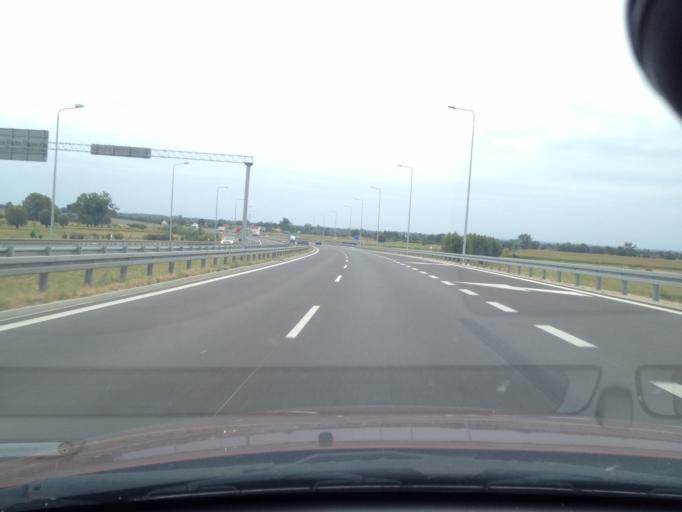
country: PL
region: Lubusz
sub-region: Powiat gorzowski
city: Jenin
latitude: 52.7103
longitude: 15.1605
